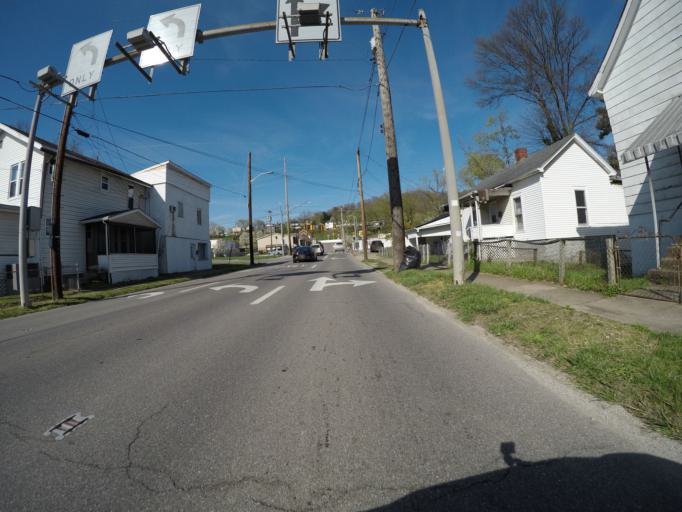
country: US
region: West Virginia
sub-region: Kanawha County
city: South Charleston
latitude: 38.3717
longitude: -81.6646
